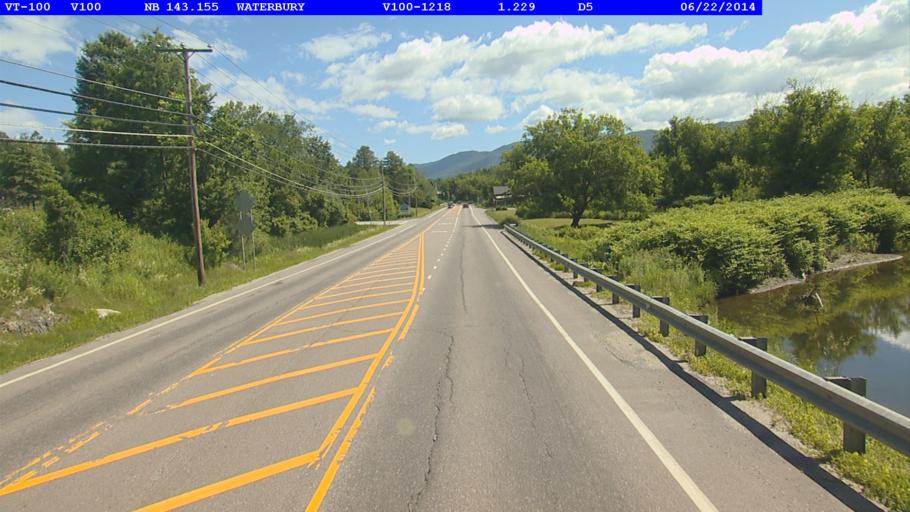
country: US
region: Vermont
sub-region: Washington County
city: Waterbury
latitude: 44.3510
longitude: -72.7406
